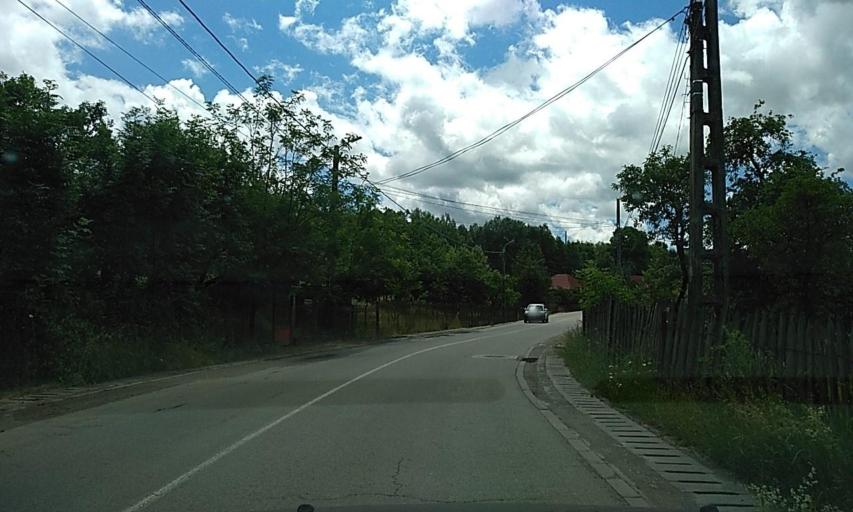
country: RO
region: Hunedoara
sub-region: Oras Petrila
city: Petrila
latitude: 45.4544
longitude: 23.4370
